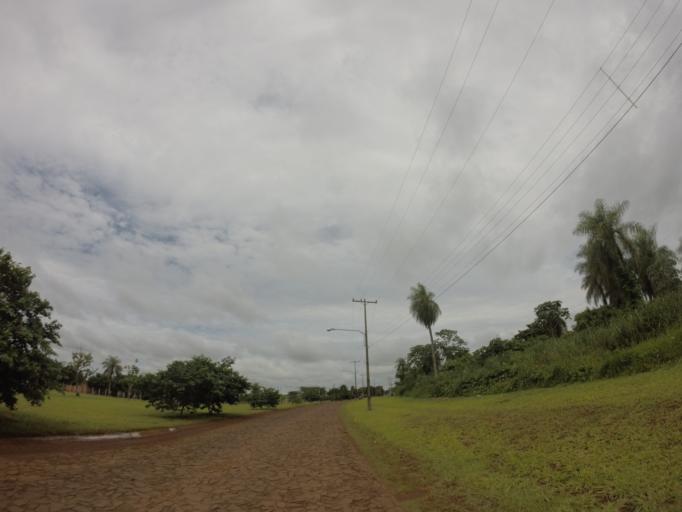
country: PY
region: Alto Parana
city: Ciudad del Este
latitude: -25.3905
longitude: -54.6244
